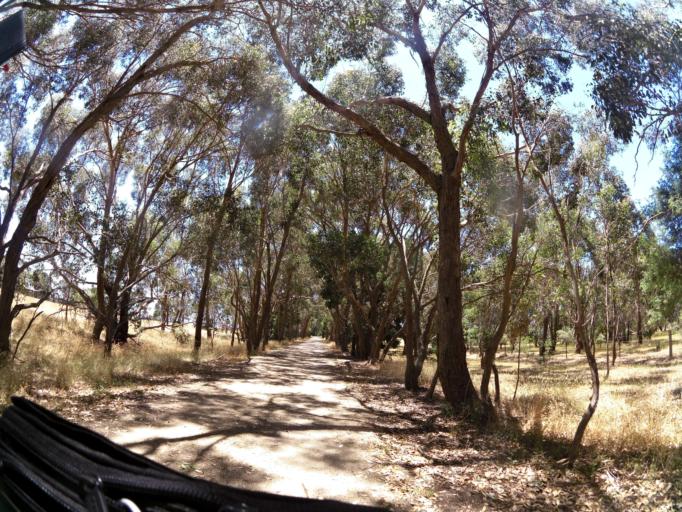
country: AU
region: Victoria
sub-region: Ballarat North
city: Delacombe
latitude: -37.5736
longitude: 143.7290
